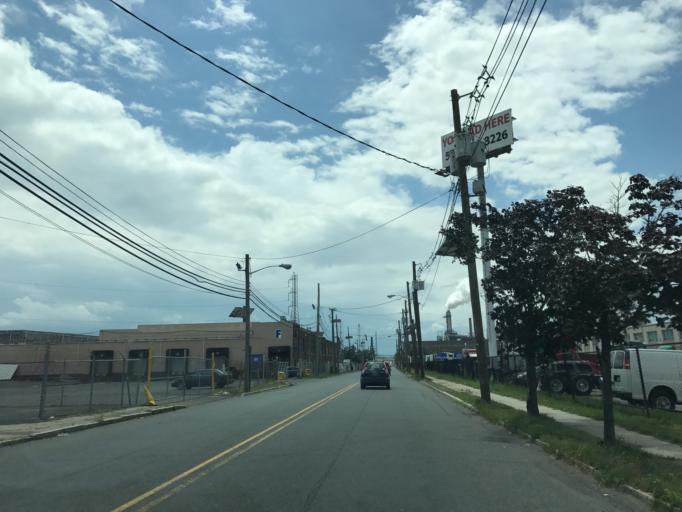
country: US
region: New Jersey
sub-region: Union County
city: Elizabeth
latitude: 40.6417
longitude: -74.2143
